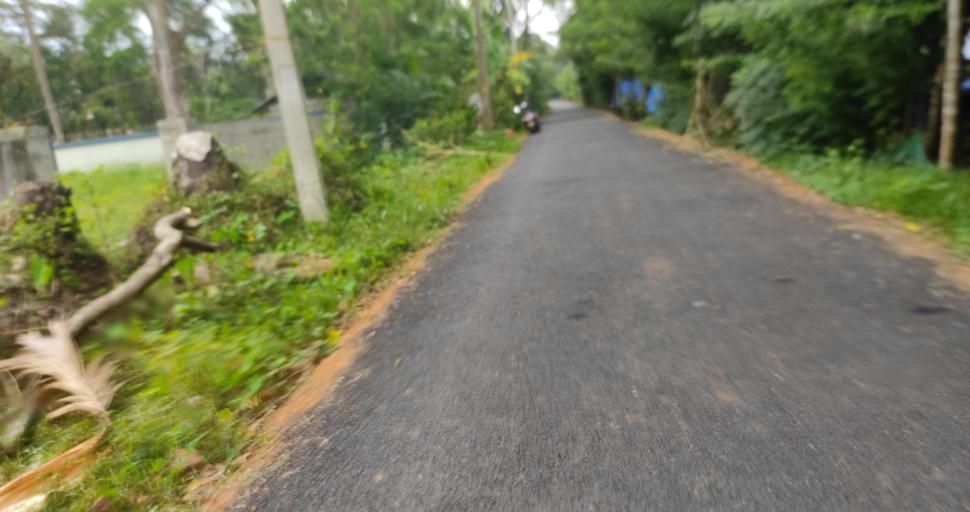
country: IN
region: Kerala
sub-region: Alappuzha
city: Shertallai
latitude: 9.6622
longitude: 76.3319
